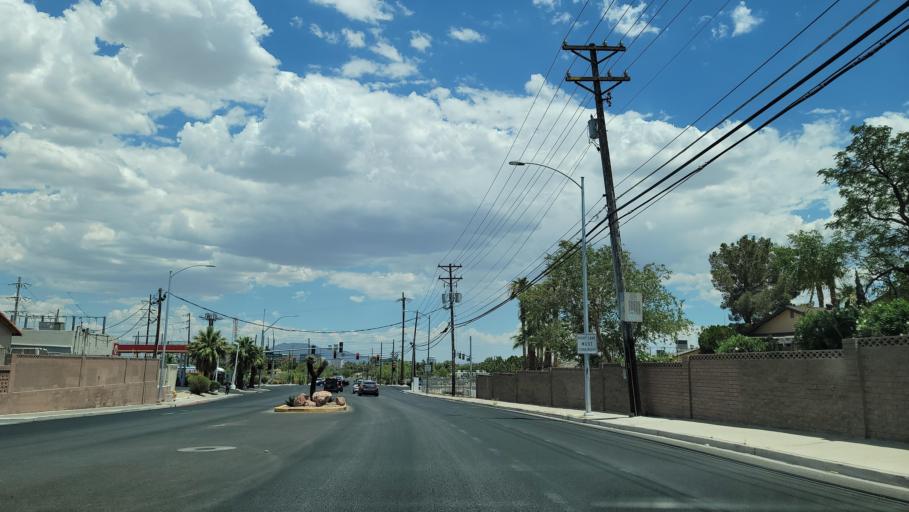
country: US
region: Nevada
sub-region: Clark County
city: Las Vegas
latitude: 36.1663
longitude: -115.1941
